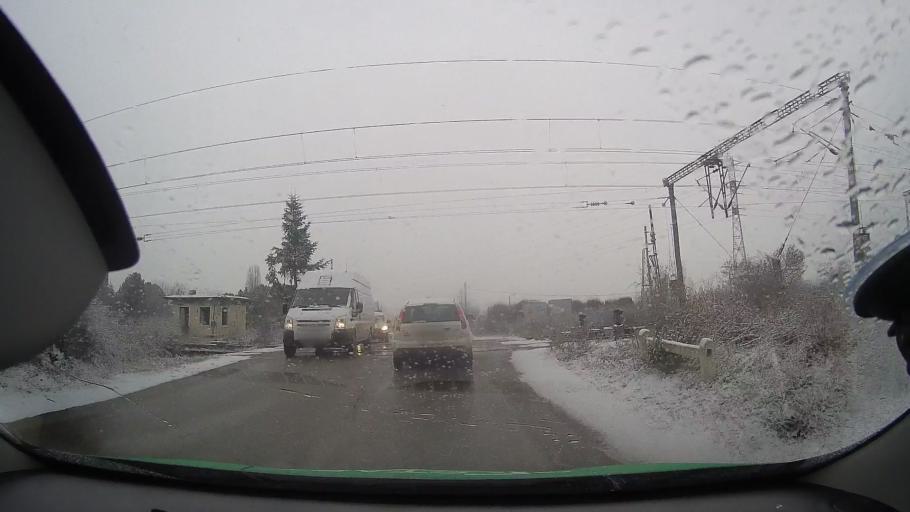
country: RO
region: Alba
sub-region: Municipiul Aiud
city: Aiud
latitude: 46.3055
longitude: 23.7334
